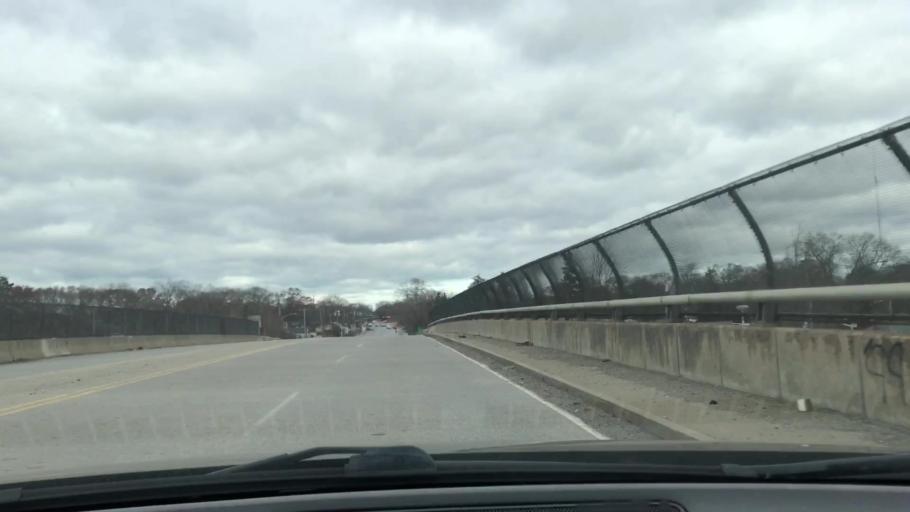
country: US
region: New York
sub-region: Suffolk County
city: Ronkonkoma
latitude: 40.8075
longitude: -73.1111
